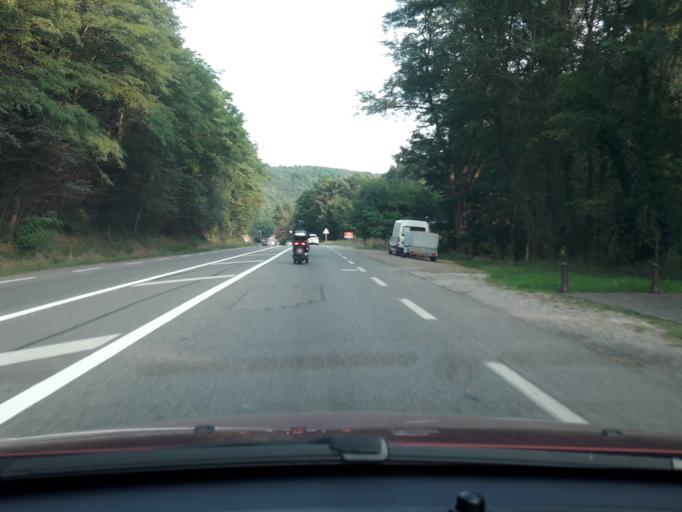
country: FR
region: Alsace
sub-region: Departement du Bas-Rhin
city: Wasselonne
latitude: 48.6335
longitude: 7.4630
